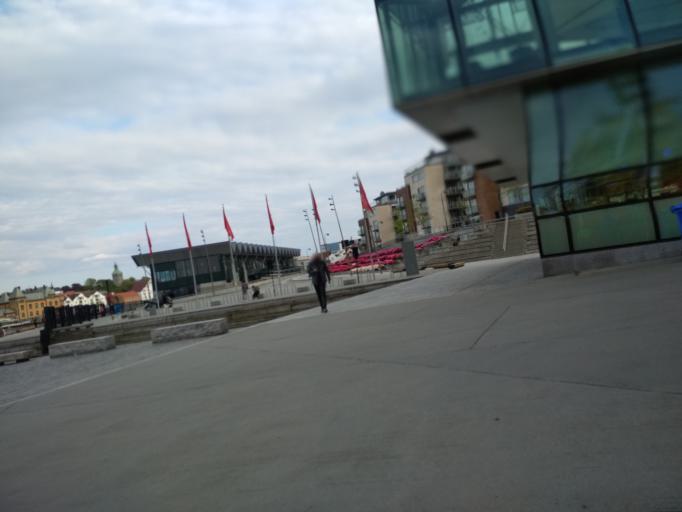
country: NO
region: Rogaland
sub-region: Stavanger
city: Stavanger
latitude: 58.9756
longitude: 5.7236
